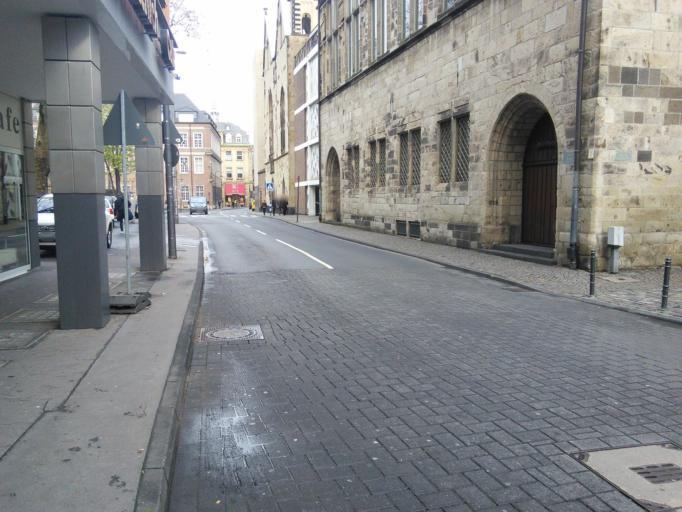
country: DE
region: North Rhine-Westphalia
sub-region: Regierungsbezirk Koln
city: Altstadt Nord
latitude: 50.9363
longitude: 6.9581
